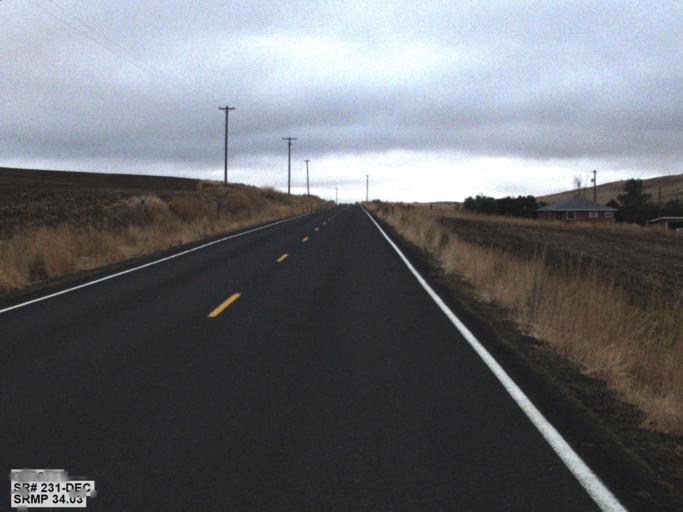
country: US
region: Washington
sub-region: Spokane County
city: Medical Lake
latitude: 47.7109
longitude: -117.8734
